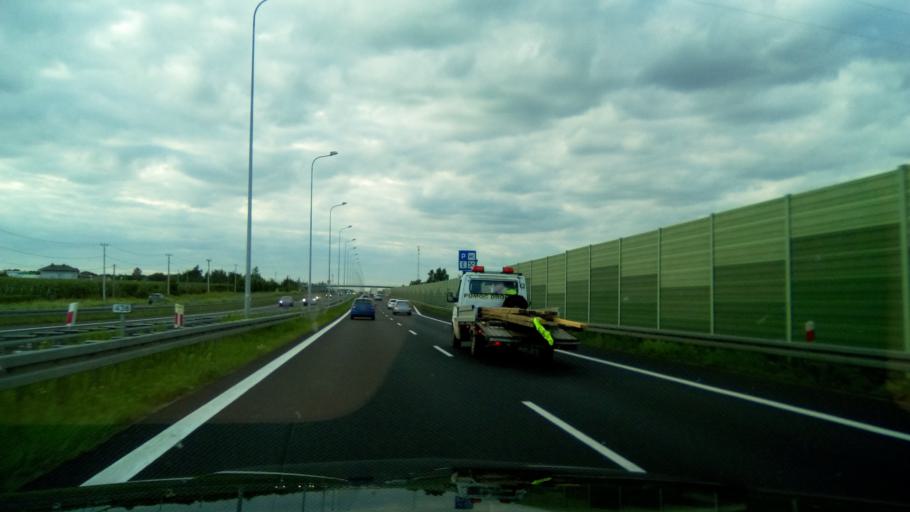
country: PL
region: Masovian Voivodeship
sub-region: Powiat bialobrzeski
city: Promna
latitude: 51.6899
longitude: 20.9344
